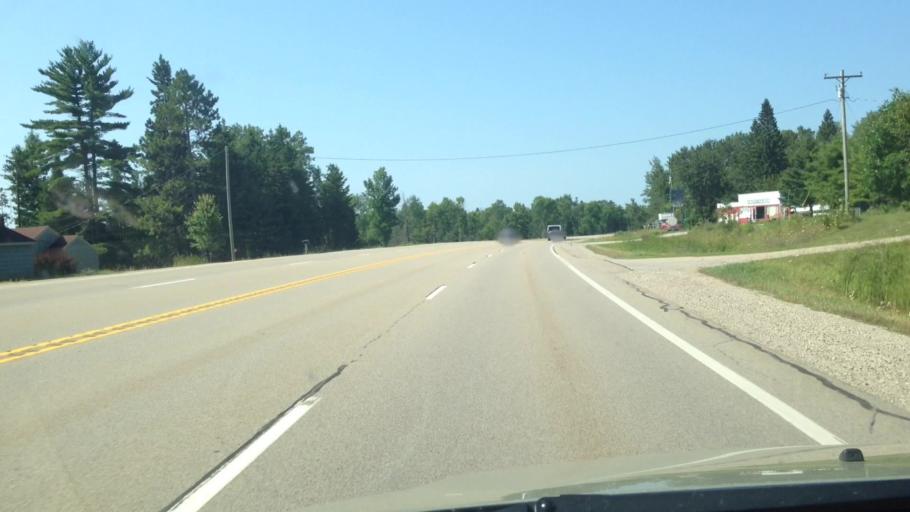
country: US
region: Michigan
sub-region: Delta County
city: Escanaba
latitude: 45.5453
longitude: -87.2725
